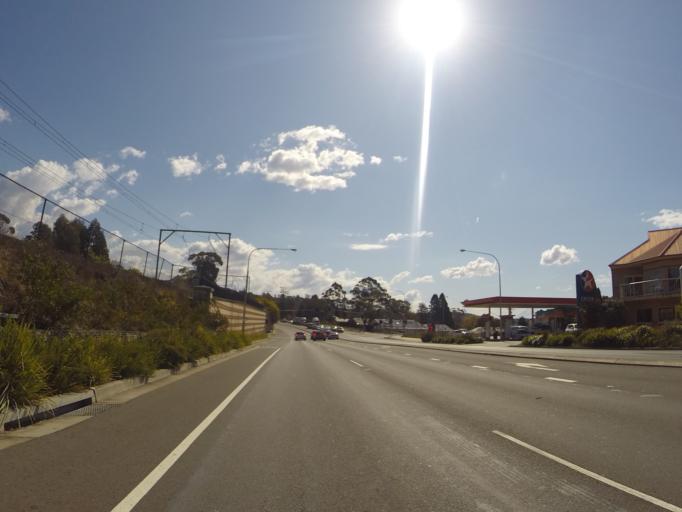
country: AU
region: New South Wales
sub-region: Blue Mountains Municipality
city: Hazelbrook
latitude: -33.7217
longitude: 150.4523
